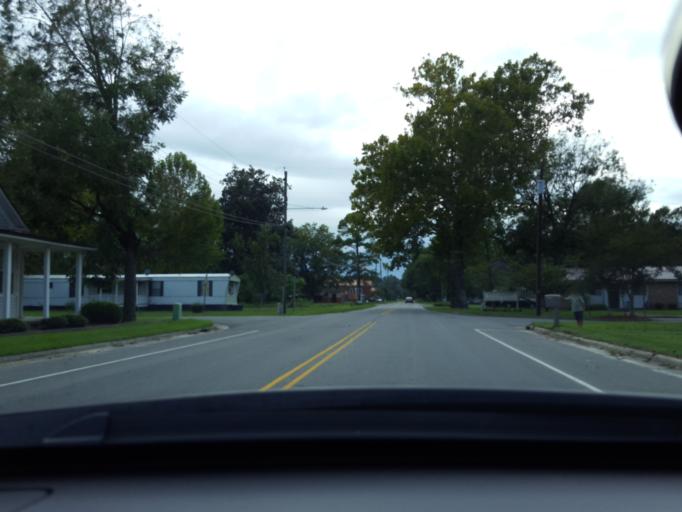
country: US
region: North Carolina
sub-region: Duplin County
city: Rose Hill
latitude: 34.8960
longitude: -78.0566
